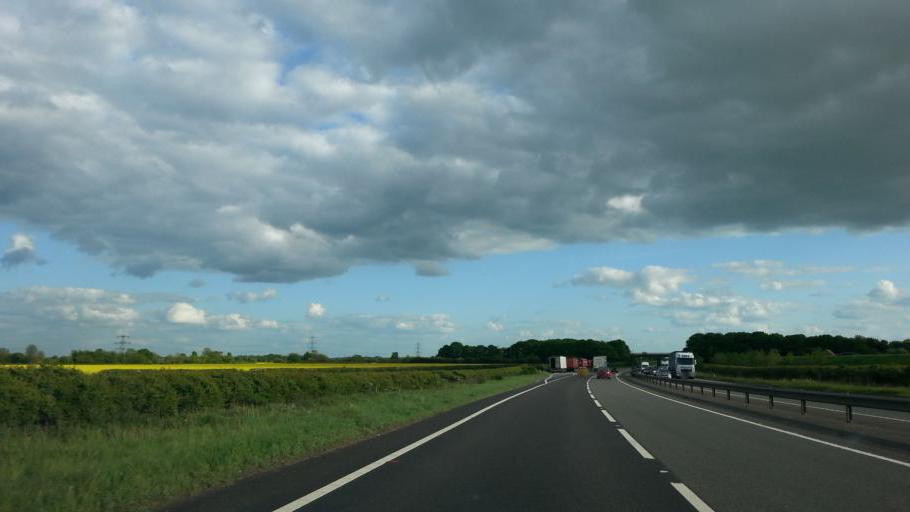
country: GB
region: England
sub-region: Nottinghamshire
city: Newark on Trent
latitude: 53.0676
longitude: -0.7660
